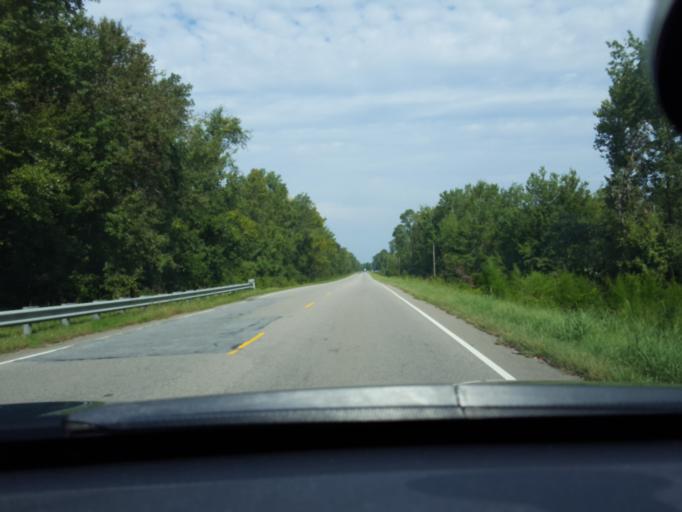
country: US
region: North Carolina
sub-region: Washington County
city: Plymouth
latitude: 35.8967
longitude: -76.7066
